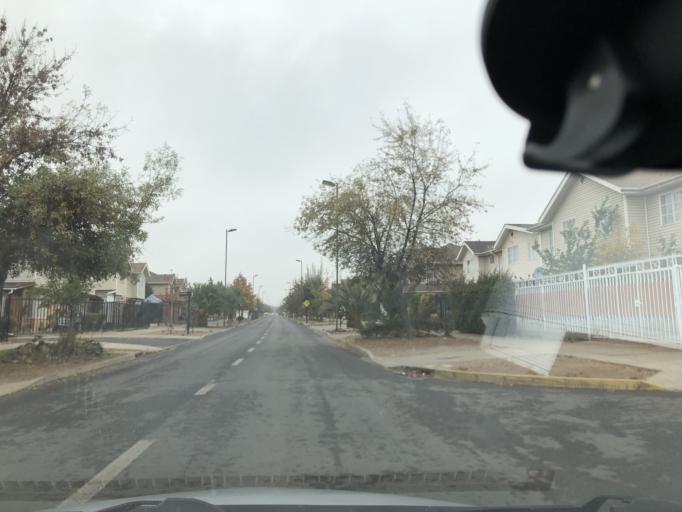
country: CL
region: Santiago Metropolitan
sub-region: Provincia de Cordillera
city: Puente Alto
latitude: -33.5930
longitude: -70.5935
